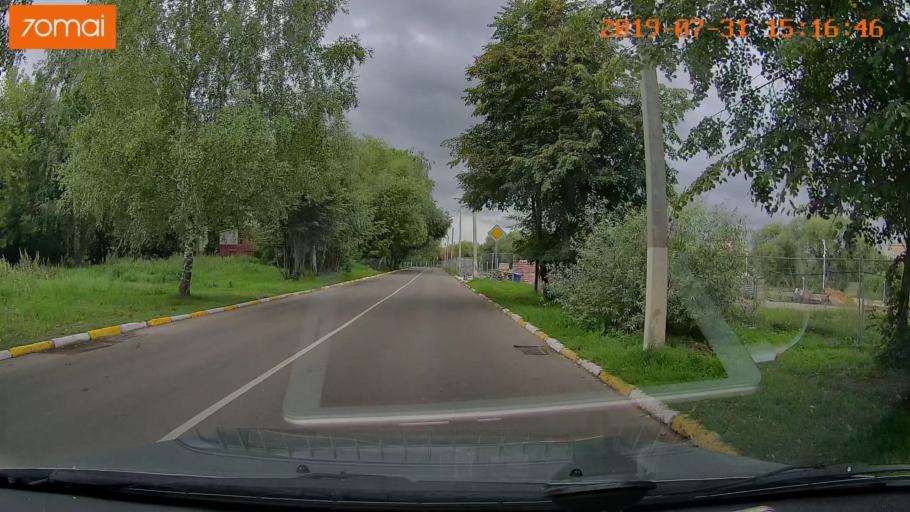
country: RU
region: Moskovskaya
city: Voskresensk
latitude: 55.3176
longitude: 38.6593
